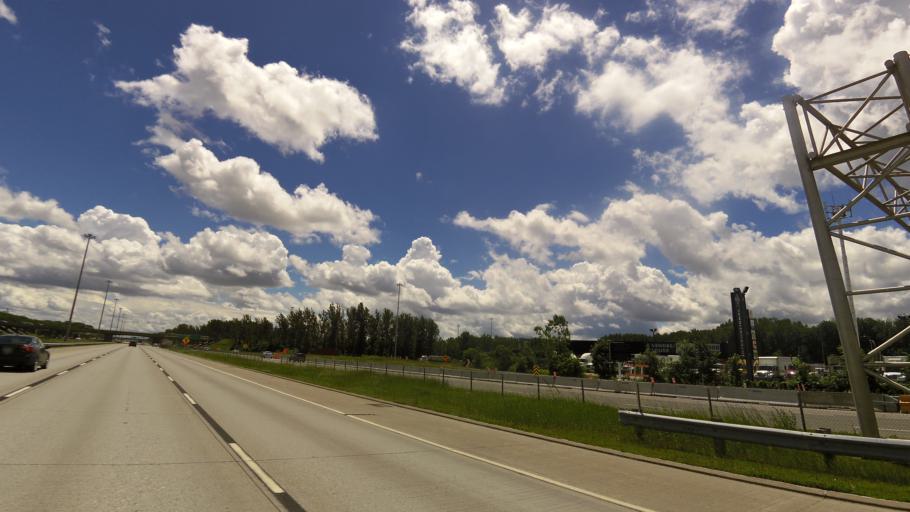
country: CA
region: Quebec
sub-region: Laurentides
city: Boisbriand
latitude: 45.5573
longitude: -73.8124
